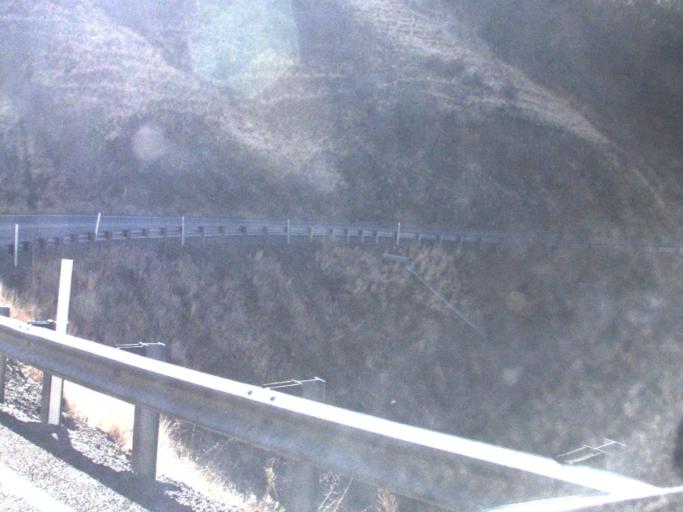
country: US
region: Washington
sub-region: Asotin County
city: Asotin
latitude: 46.0648
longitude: -117.2288
